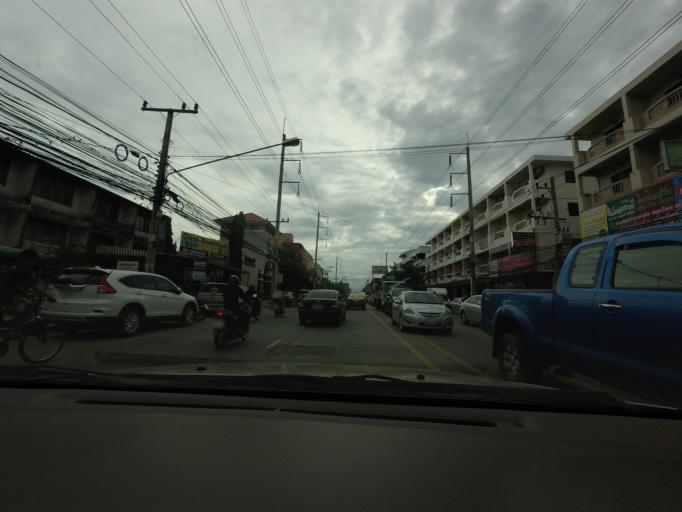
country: TH
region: Chon Buri
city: Phatthaya
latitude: 12.9090
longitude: 100.8929
